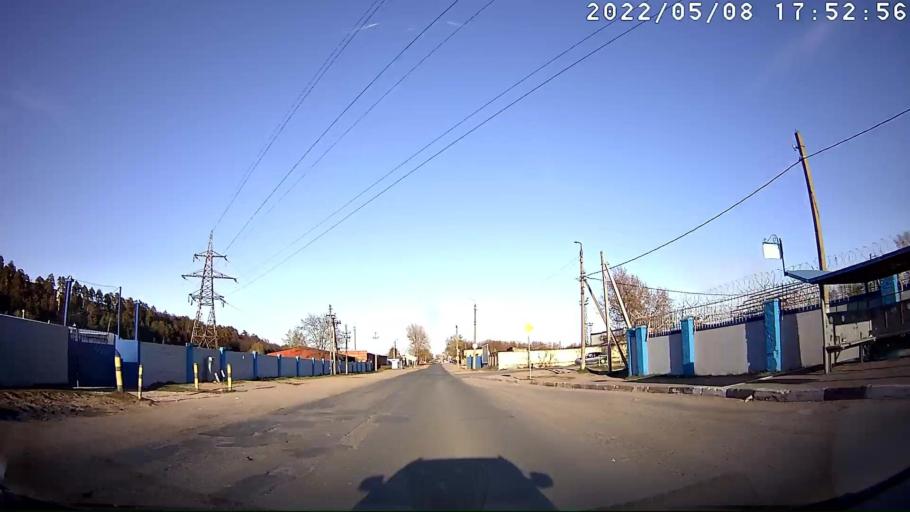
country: RU
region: Tatarstan
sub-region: Zelenodol'skiy Rayon
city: Zelenodolsk
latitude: 55.8402
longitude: 48.5109
